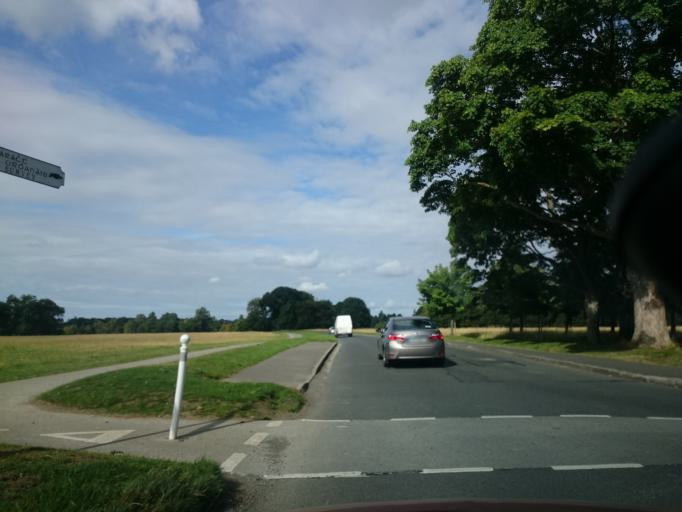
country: IE
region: Leinster
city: Chapelizod
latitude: 53.3693
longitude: -6.3340
